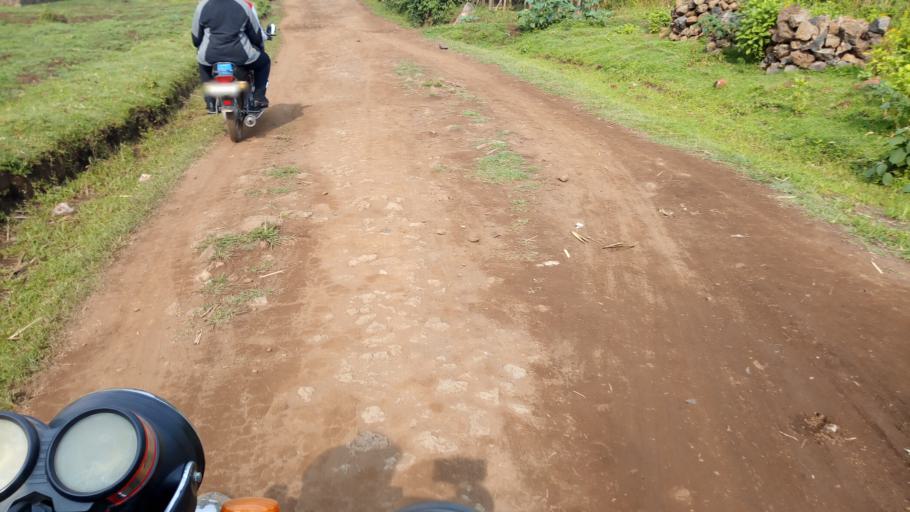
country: UG
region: Western Region
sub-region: Kisoro District
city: Kisoro
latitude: -1.3116
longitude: 29.6535
